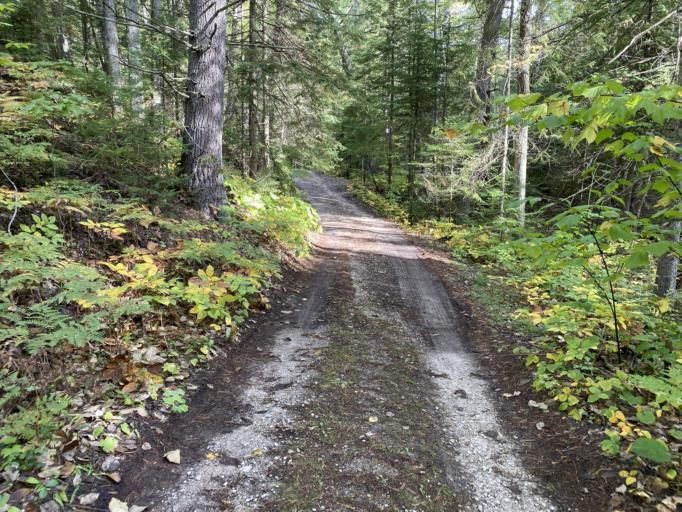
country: US
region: Michigan
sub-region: Mackinac County
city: Saint Ignace
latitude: 45.7461
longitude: -84.8786
